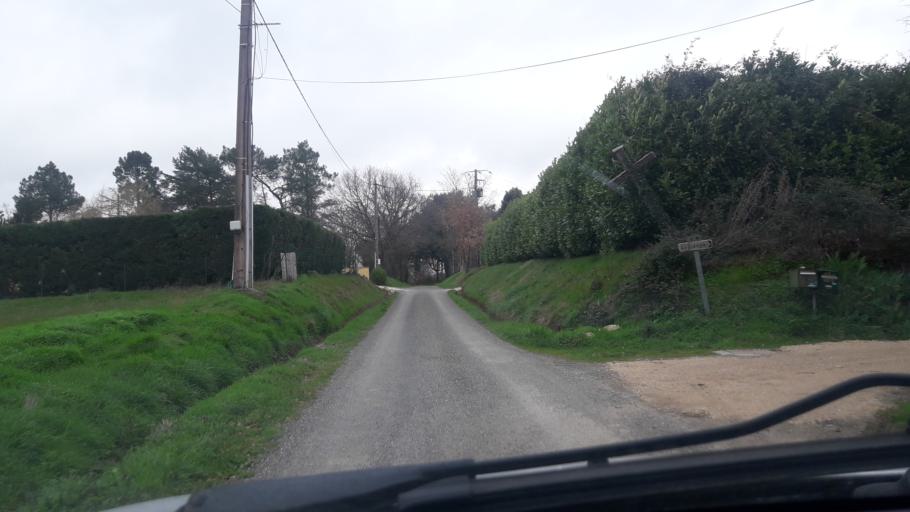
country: FR
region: Midi-Pyrenees
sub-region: Departement du Gers
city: Gimont
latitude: 43.6469
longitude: 0.9747
